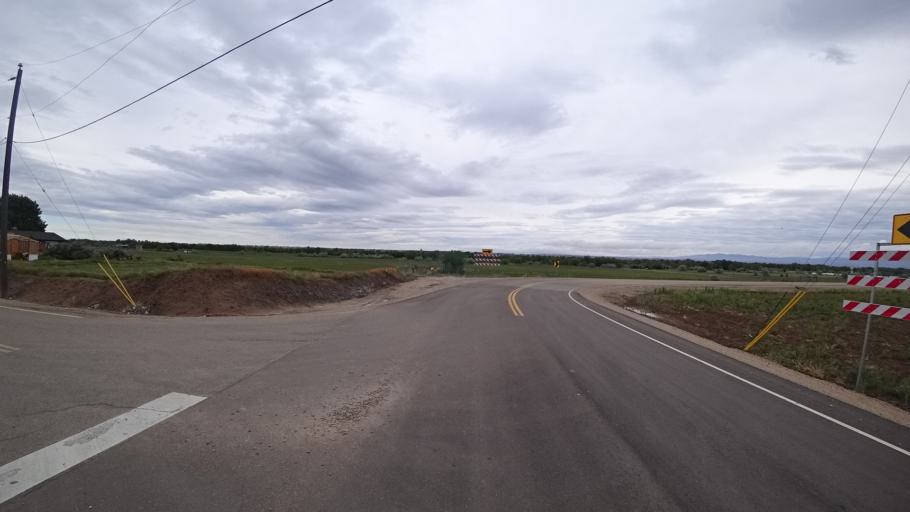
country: US
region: Idaho
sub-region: Ada County
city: Star
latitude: 43.6704
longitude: -116.5126
